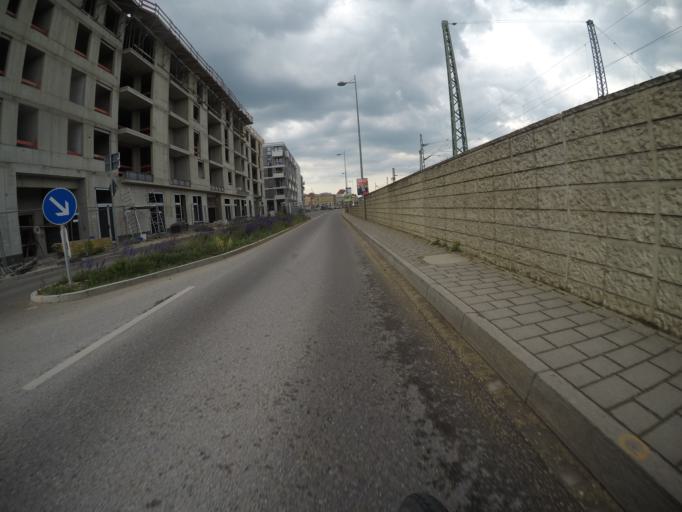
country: DE
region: Baden-Wuerttemberg
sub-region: Regierungsbezirk Stuttgart
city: Esslingen
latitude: 48.7405
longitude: 9.2986
